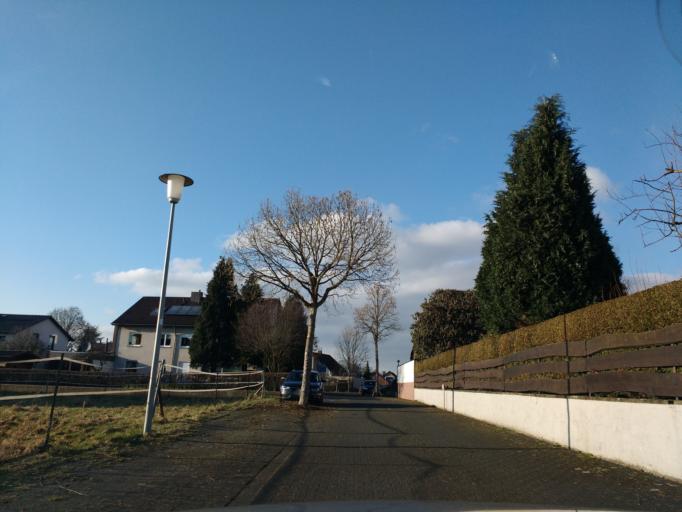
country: DE
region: North Rhine-Westphalia
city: Bad Lippspringe
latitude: 51.7480
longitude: 8.8482
